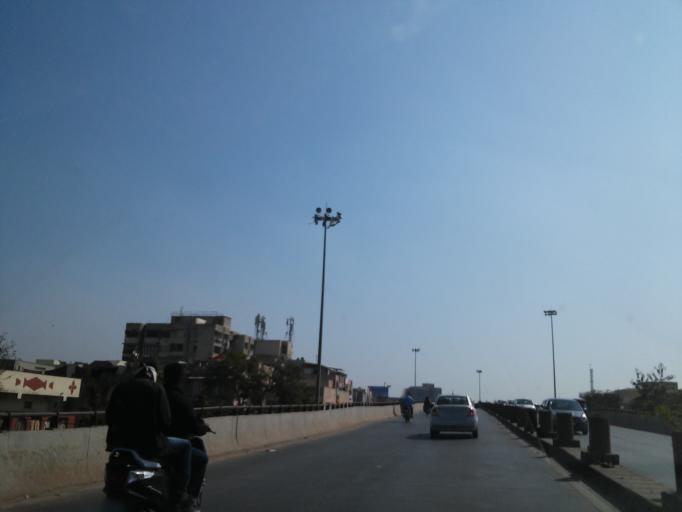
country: IN
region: Gujarat
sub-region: Ahmadabad
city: Ahmedabad
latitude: 23.0158
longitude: 72.5447
